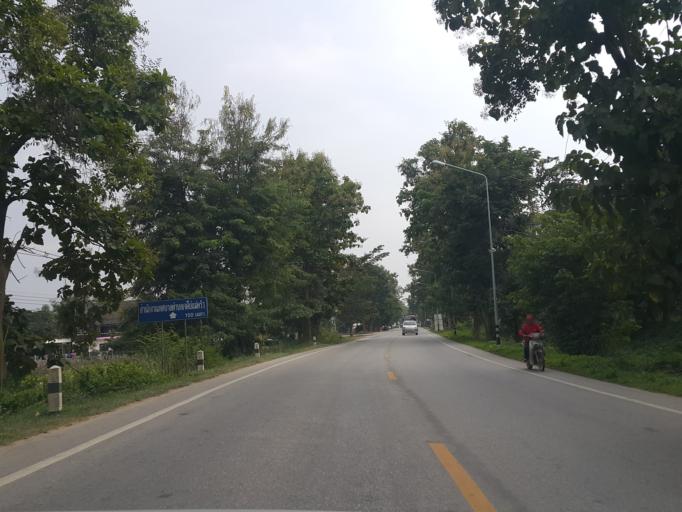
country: TH
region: Chiang Mai
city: Mae Taeng
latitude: 18.9982
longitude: 98.9766
